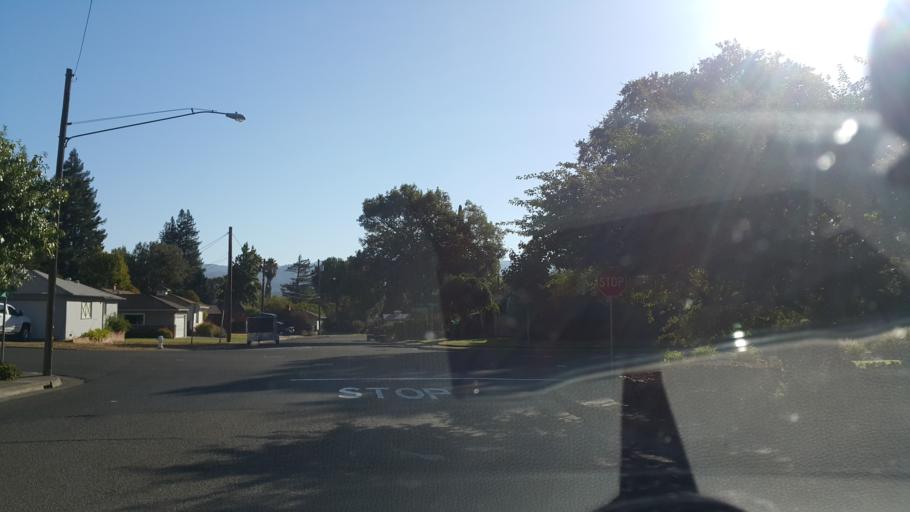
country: US
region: California
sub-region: Mendocino County
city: Ukiah
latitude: 39.1434
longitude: -123.2132
